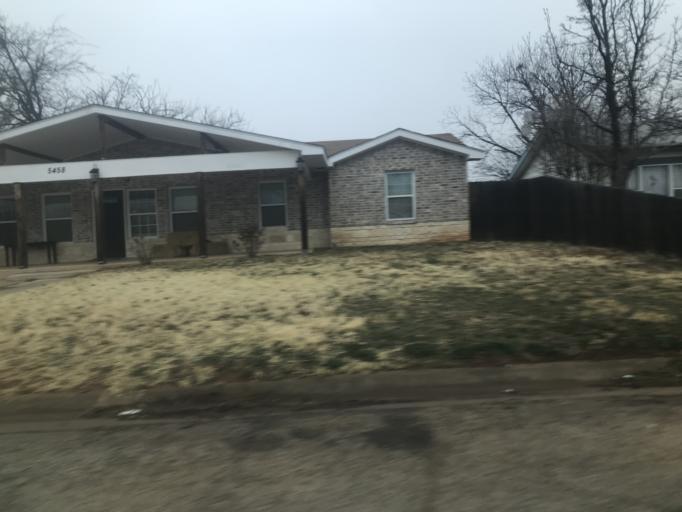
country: US
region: Texas
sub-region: Taylor County
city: Abilene
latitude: 32.4460
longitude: -99.7961
